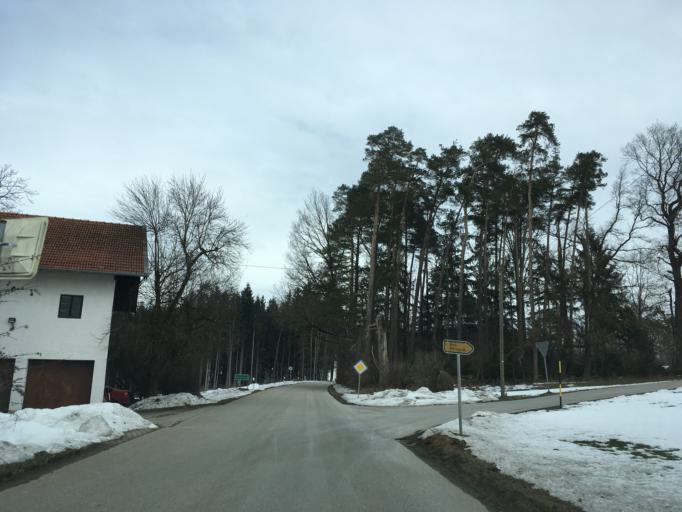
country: DE
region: Bavaria
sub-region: Upper Bavaria
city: Jettenbach
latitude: 48.1310
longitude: 12.3869
